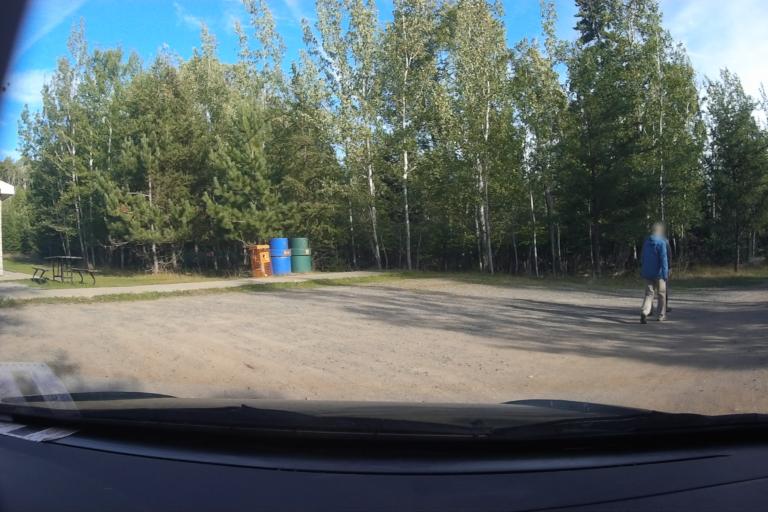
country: CA
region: Ontario
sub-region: Thunder Bay District
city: Thunder Bay
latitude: 48.3678
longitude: -88.8029
